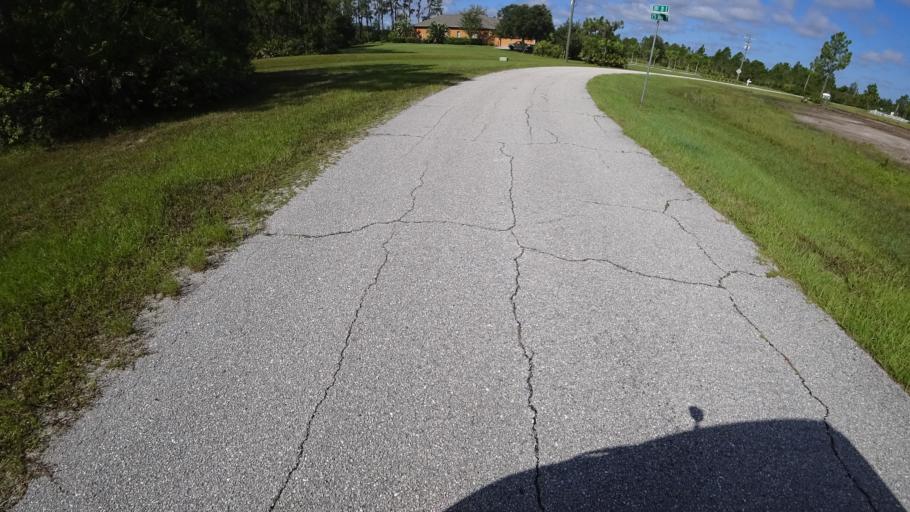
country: US
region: Florida
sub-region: Sarasota County
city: The Meadows
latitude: 27.4063
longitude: -82.3369
